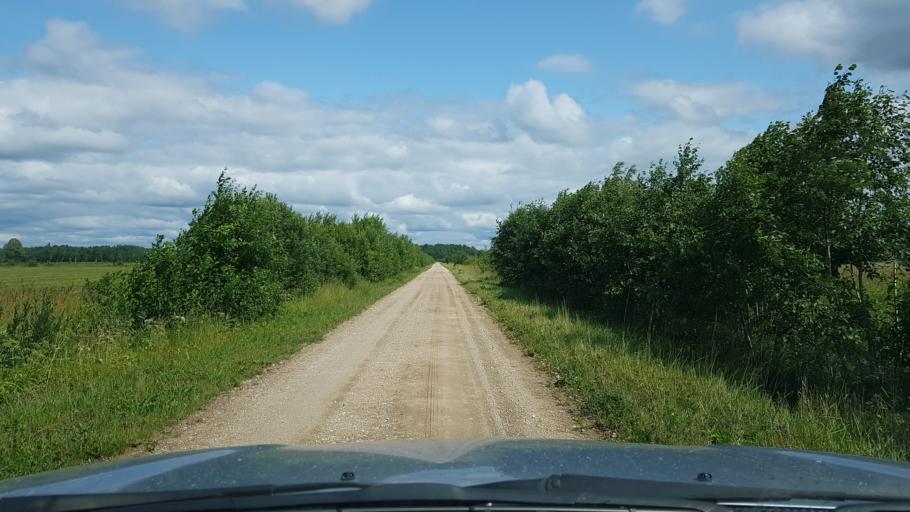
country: EE
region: Ida-Virumaa
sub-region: Sillamaee linn
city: Sillamae
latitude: 59.3703
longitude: 27.9119
